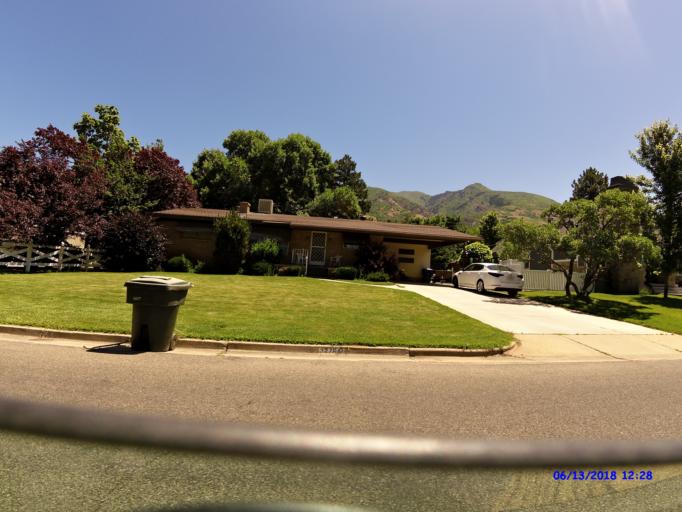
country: US
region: Utah
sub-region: Weber County
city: South Ogden
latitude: 41.2035
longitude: -111.9448
